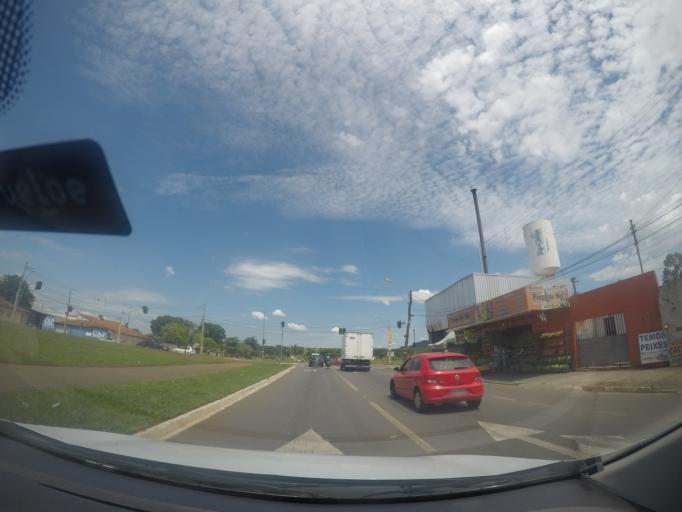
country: BR
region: Goias
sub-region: Goiania
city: Goiania
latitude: -16.6822
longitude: -49.3329
